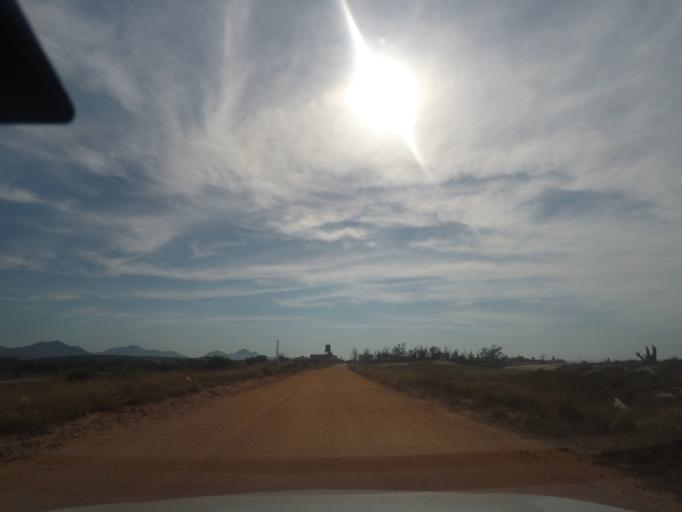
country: BR
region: Rio de Janeiro
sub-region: Marica
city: Marica
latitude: -22.9594
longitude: -42.8313
